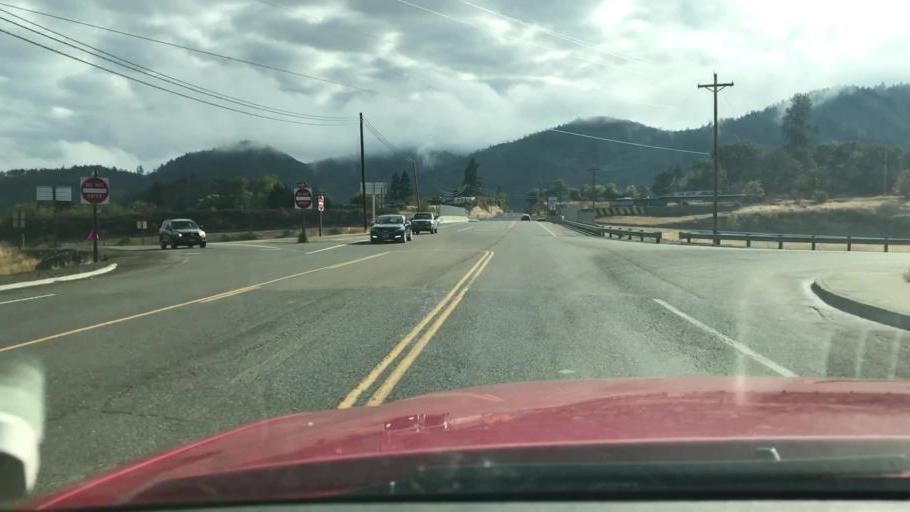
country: US
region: Oregon
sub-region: Douglas County
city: Tri-City
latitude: 42.9733
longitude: -123.3380
